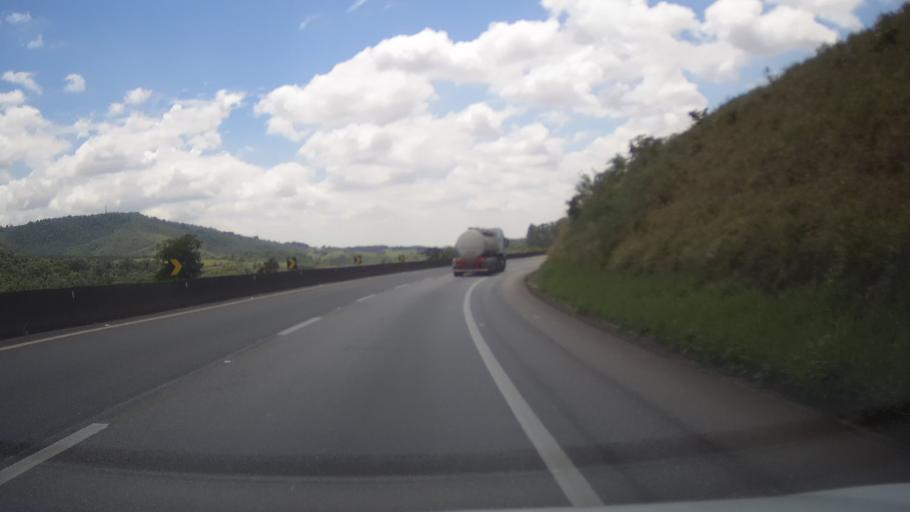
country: BR
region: Minas Gerais
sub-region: Campanha
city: Campanha
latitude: -21.8099
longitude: -45.4880
